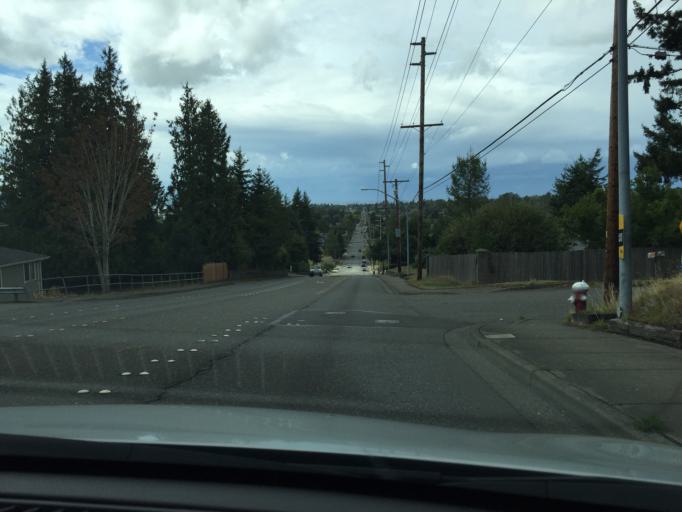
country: US
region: Washington
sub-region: Whatcom County
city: Geneva
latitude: 48.7631
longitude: -122.4339
